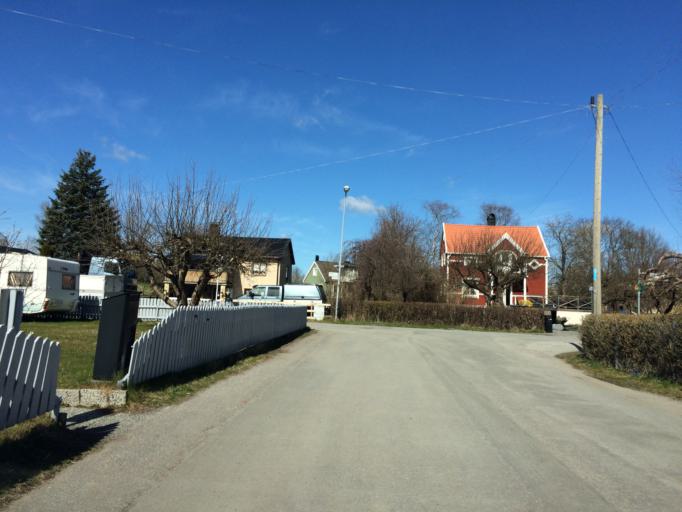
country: SE
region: Stockholm
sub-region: Sollentuna Kommun
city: Sollentuna
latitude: 59.4580
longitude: 17.9143
